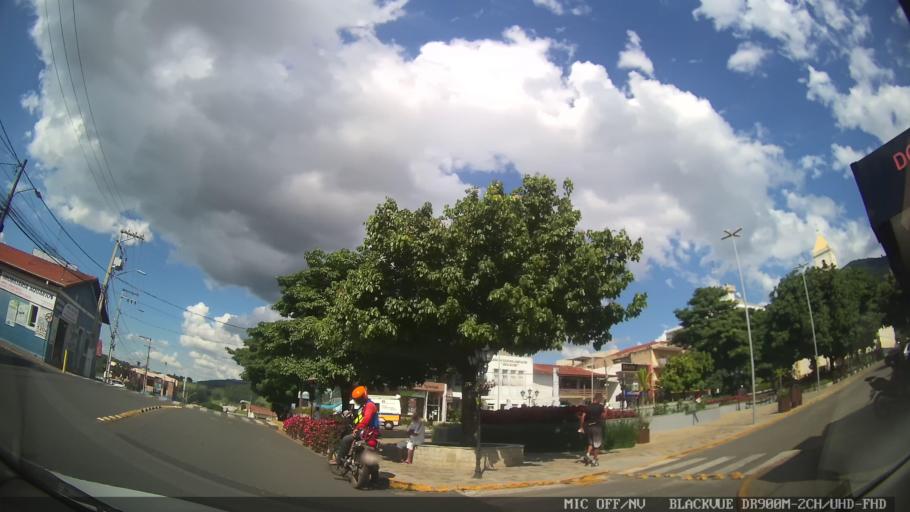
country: BR
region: Minas Gerais
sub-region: Extrema
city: Extrema
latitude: -22.8546
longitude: -46.3194
